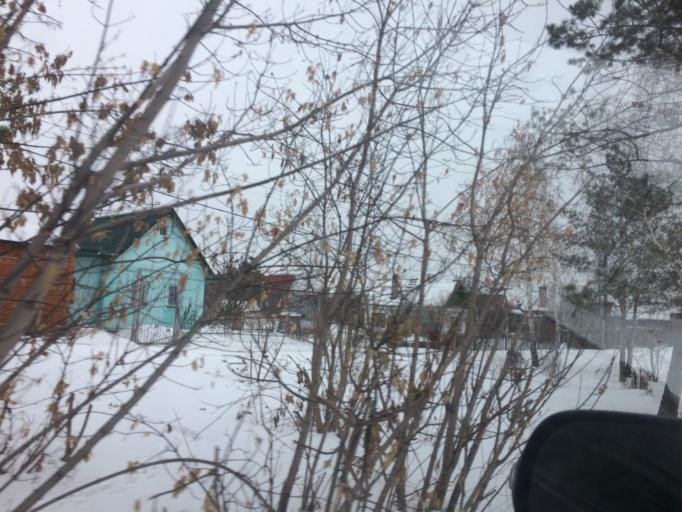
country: RU
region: Chelyabinsk
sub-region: Gorod Magnitogorsk
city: Magnitogorsk
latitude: 53.3578
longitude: 58.9868
